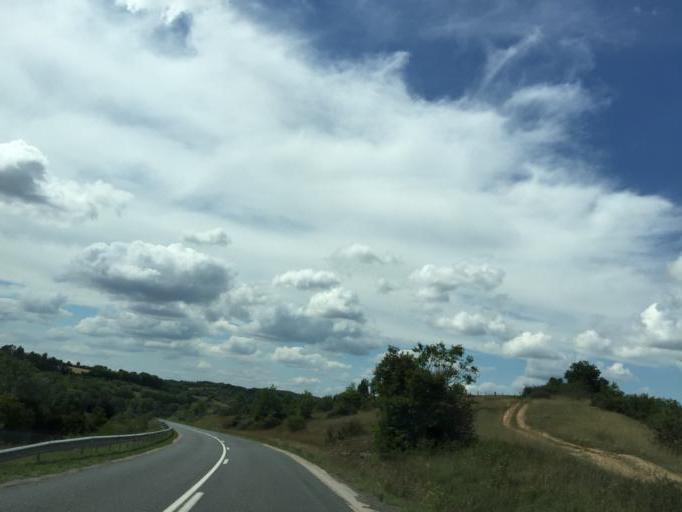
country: FR
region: Midi-Pyrenees
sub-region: Departement de l'Aveyron
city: Salles-la-Source
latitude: 44.4181
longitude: 2.5438
